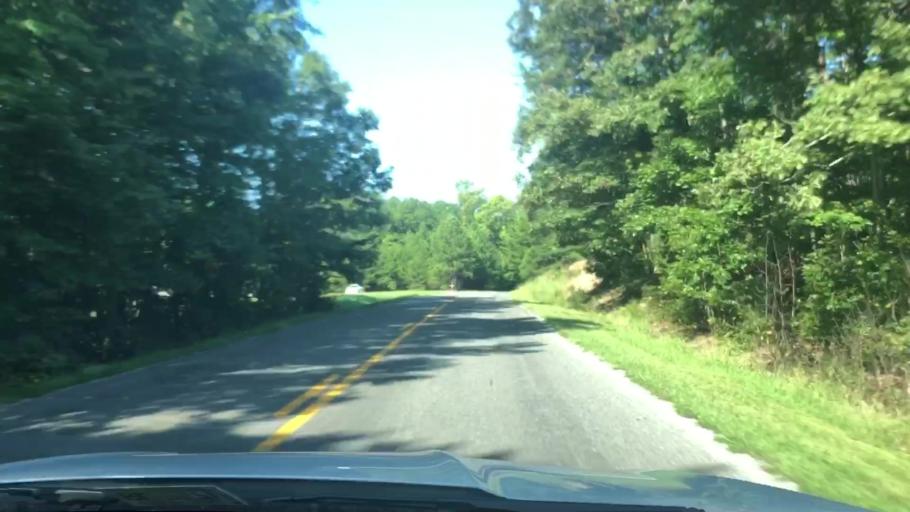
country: US
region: Virginia
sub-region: New Kent County
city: New Kent
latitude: 37.4835
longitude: -76.9242
